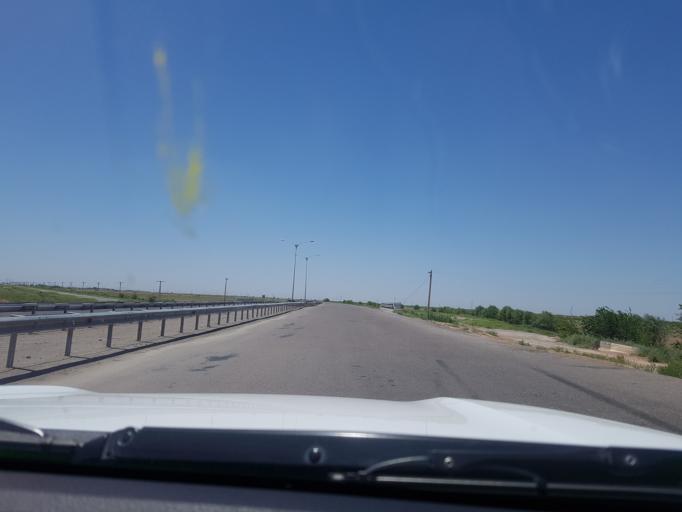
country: TM
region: Mary
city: Mary
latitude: 37.2598
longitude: 61.2566
